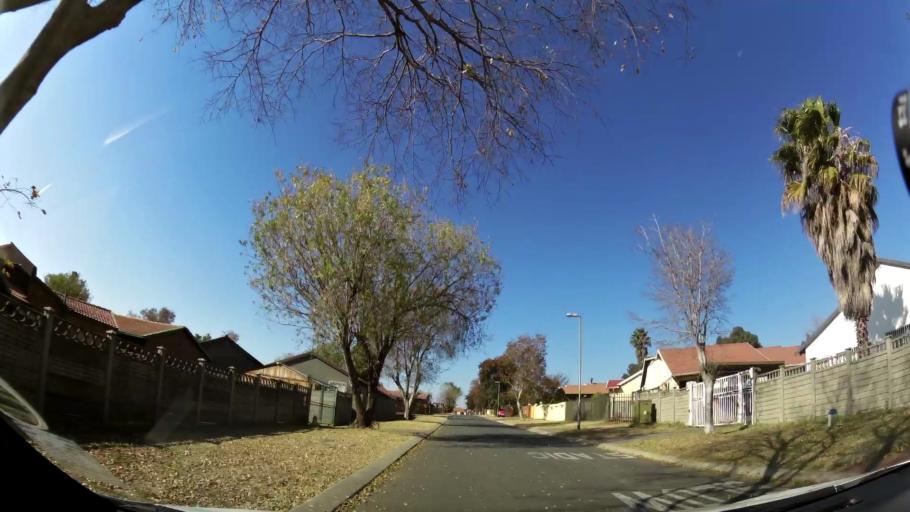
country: ZA
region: Gauteng
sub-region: City of Johannesburg Metropolitan Municipality
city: Johannesburg
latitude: -26.2396
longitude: 28.1008
